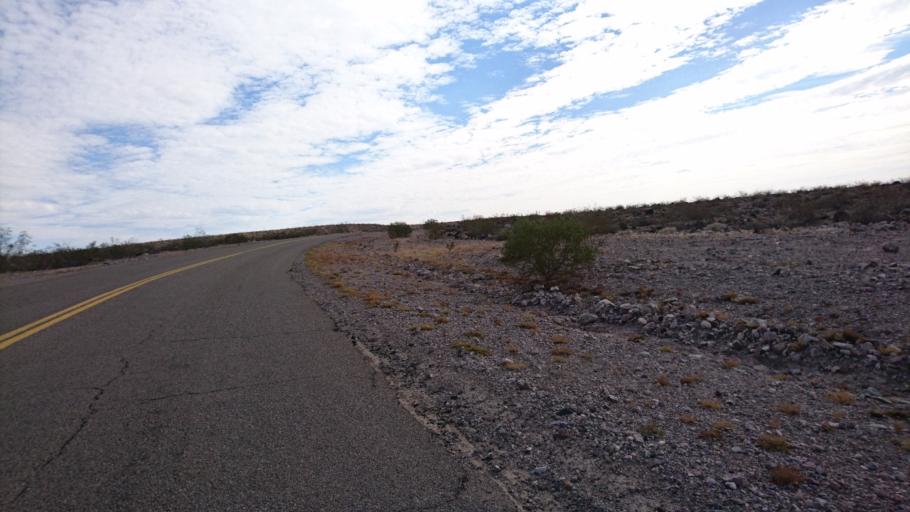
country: US
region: Arizona
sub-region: Mohave County
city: Mohave Valley
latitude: 34.9034
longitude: -114.4281
